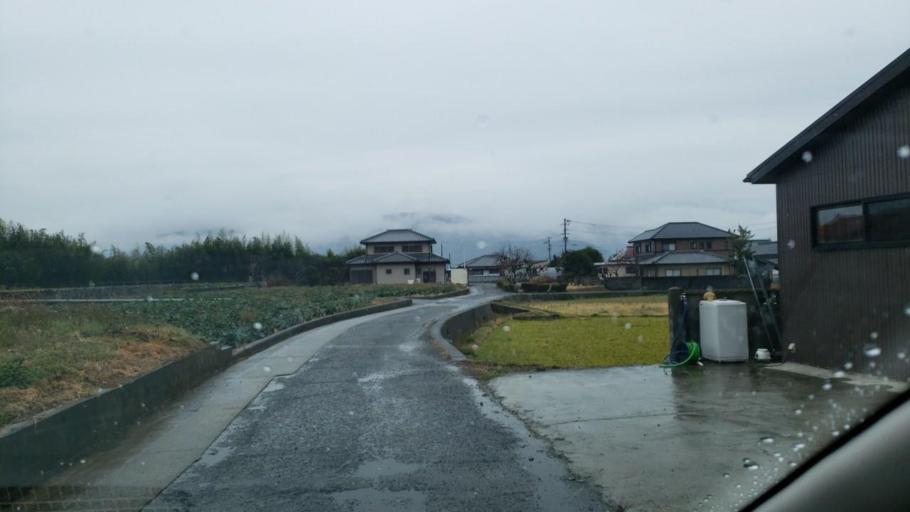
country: JP
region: Tokushima
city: Kamojimacho-jogejima
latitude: 34.0789
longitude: 134.2567
